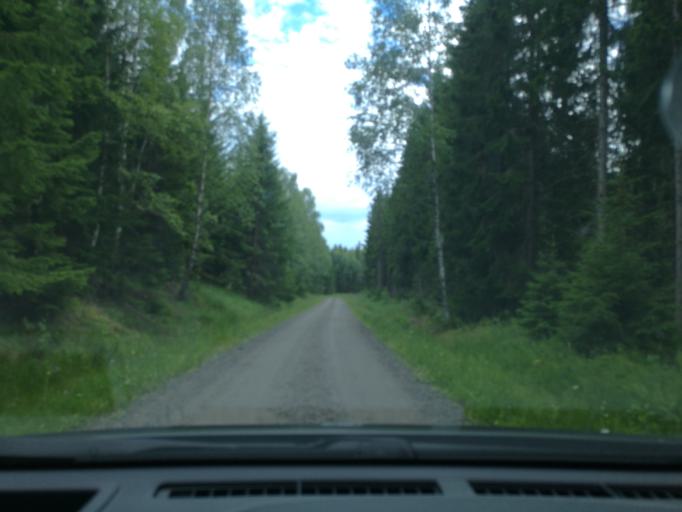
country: SE
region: Vaestmanland
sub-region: Surahammars Kommun
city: Ramnas
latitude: 59.8072
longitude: 16.3084
